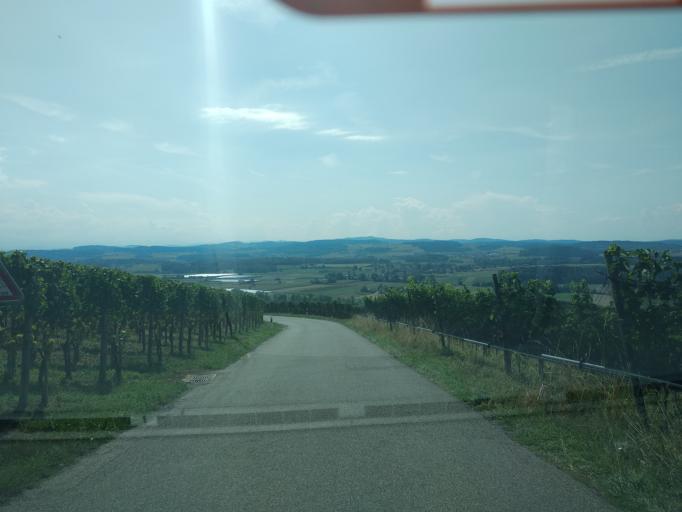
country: CH
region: Thurgau
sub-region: Frauenfeld District
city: Huttwilen
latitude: 47.5869
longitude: 8.8217
